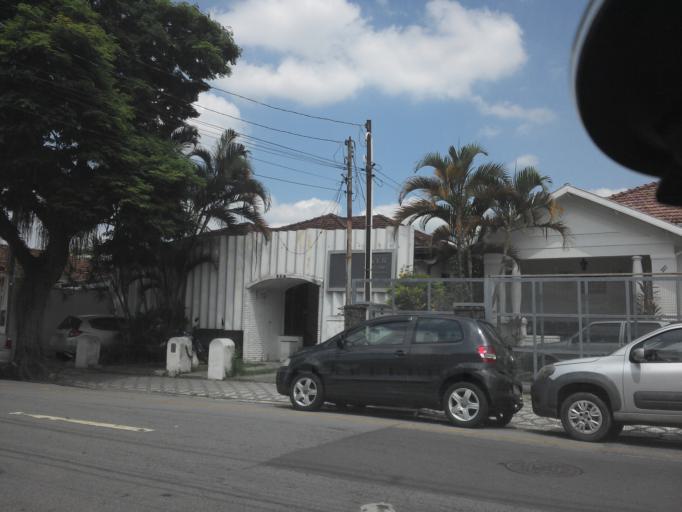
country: BR
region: Sao Paulo
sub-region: Taubate
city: Taubate
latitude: -23.0229
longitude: -45.5552
